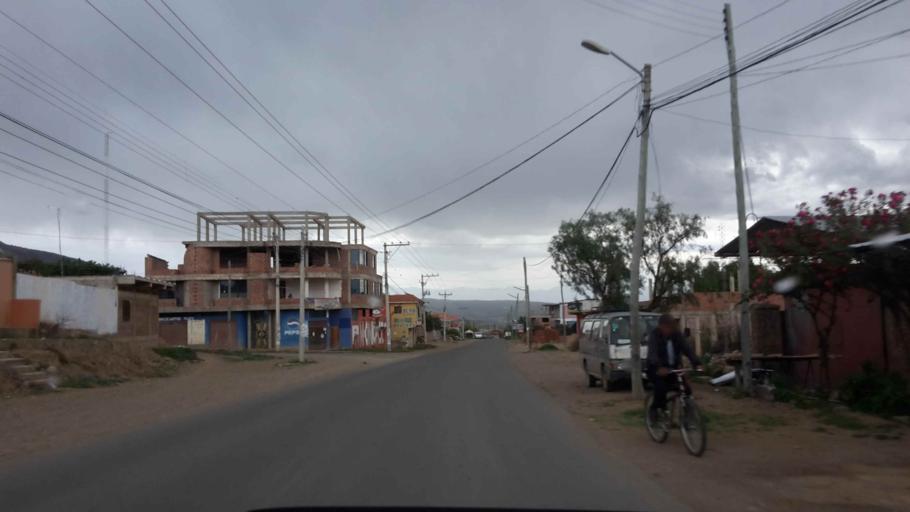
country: BO
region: Cochabamba
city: Tarata
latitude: -17.6079
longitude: -66.0284
